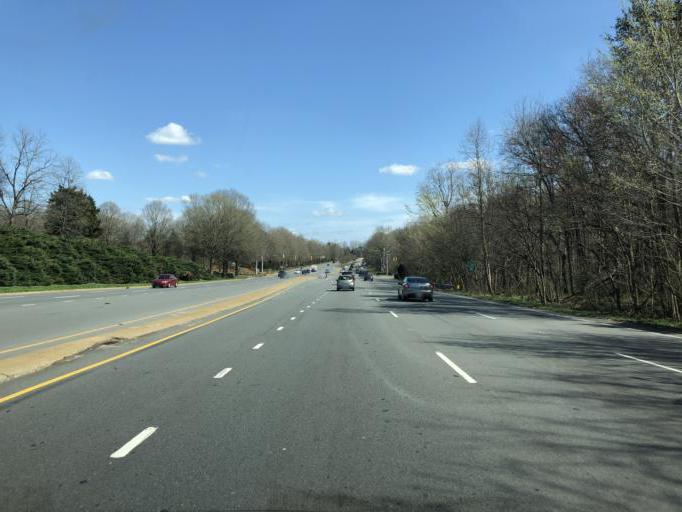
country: US
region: North Carolina
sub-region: Cabarrus County
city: Harrisburg
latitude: 35.3146
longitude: -80.7660
